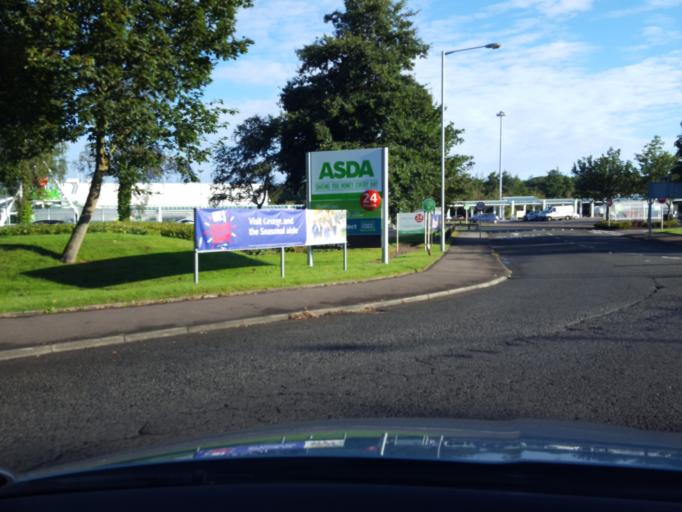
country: GB
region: Scotland
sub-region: Fife
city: Townhill
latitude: 56.0800
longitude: -3.4127
